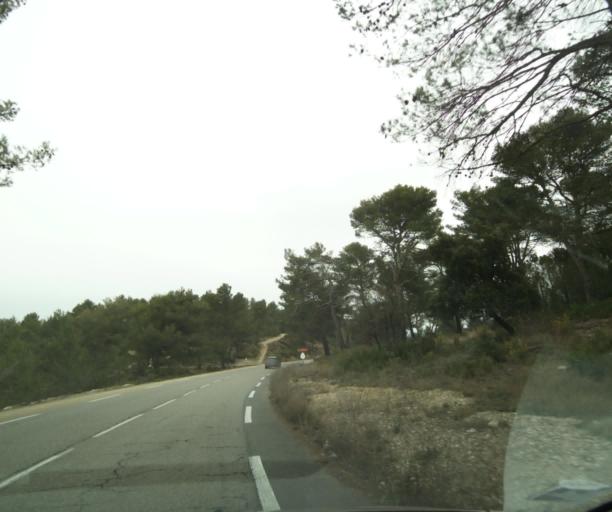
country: FR
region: Provence-Alpes-Cote d'Azur
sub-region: Departement des Bouches-du-Rhone
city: Belcodene
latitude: 43.4237
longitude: 5.6172
